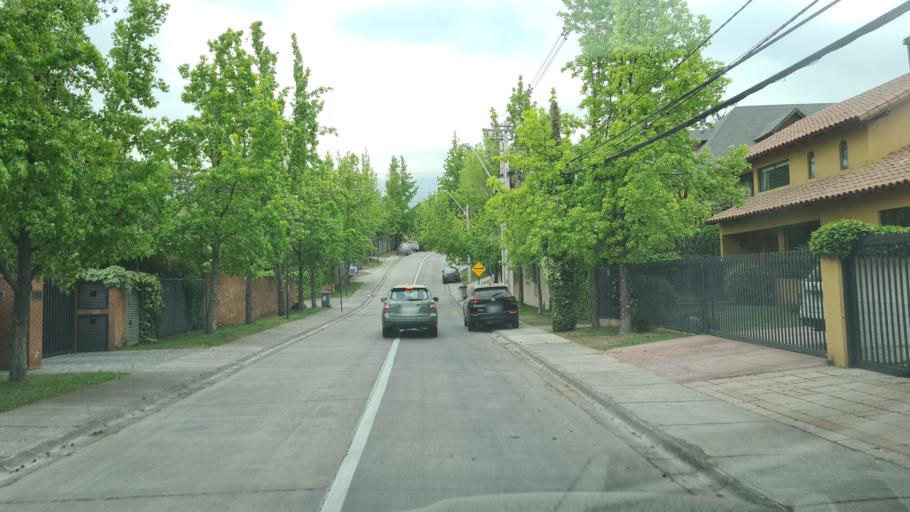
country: CL
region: Santiago Metropolitan
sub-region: Provincia de Santiago
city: Villa Presidente Frei, Nunoa, Santiago, Chile
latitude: -33.3402
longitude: -70.5065
